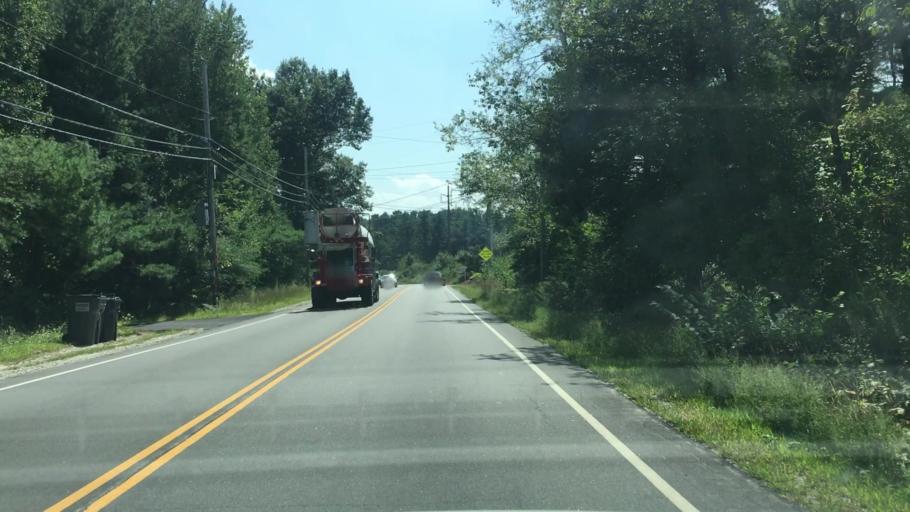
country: US
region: New Hampshire
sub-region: Rockingham County
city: Windham
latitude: 42.7885
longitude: -71.3559
